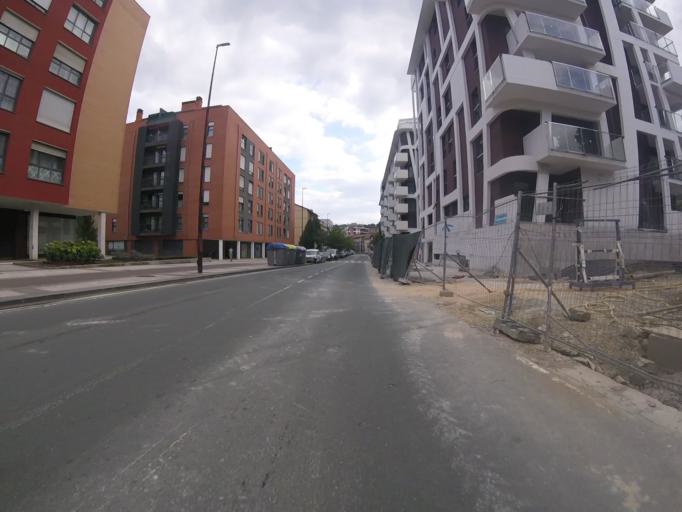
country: ES
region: Basque Country
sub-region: Provincia de Guipuzcoa
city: Andoain
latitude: 43.2110
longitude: -2.0277
